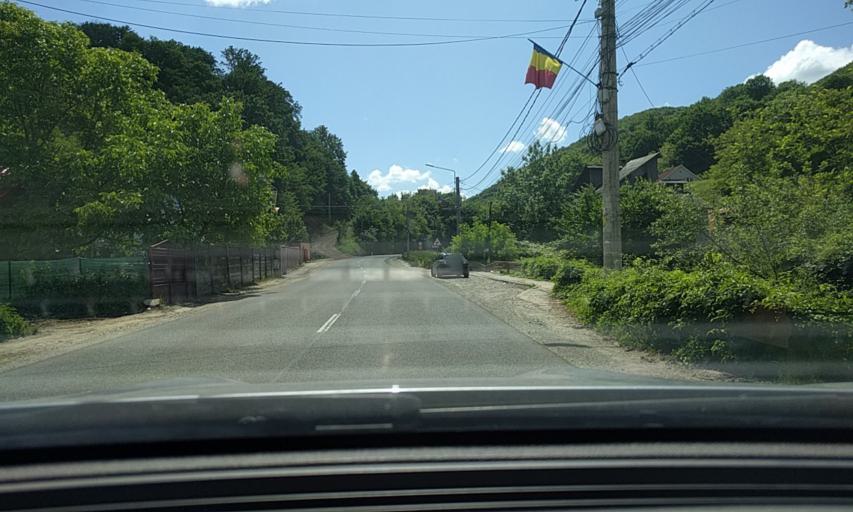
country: RO
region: Bistrita-Nasaud
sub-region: Oras Nasaud
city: Nasaud
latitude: 47.2785
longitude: 24.4217
